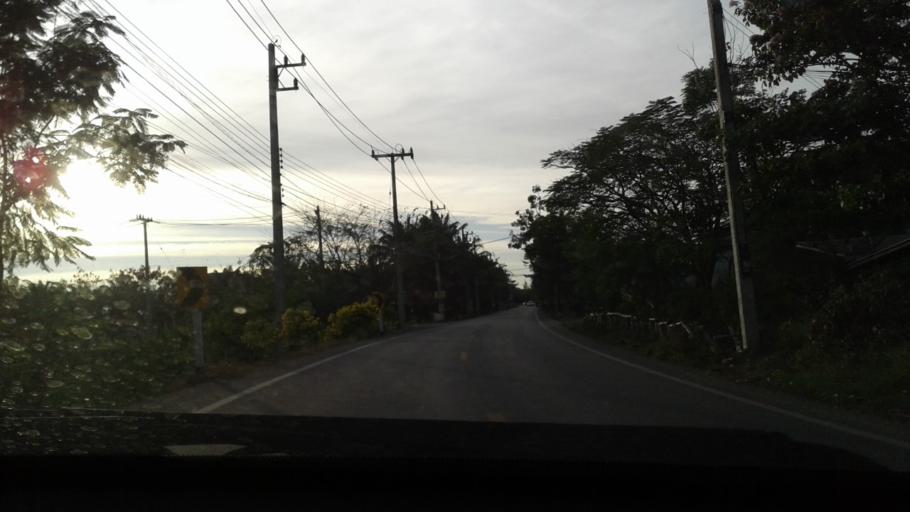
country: TH
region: Nonthaburi
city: Sai Noi
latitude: 13.9035
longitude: 100.2540
